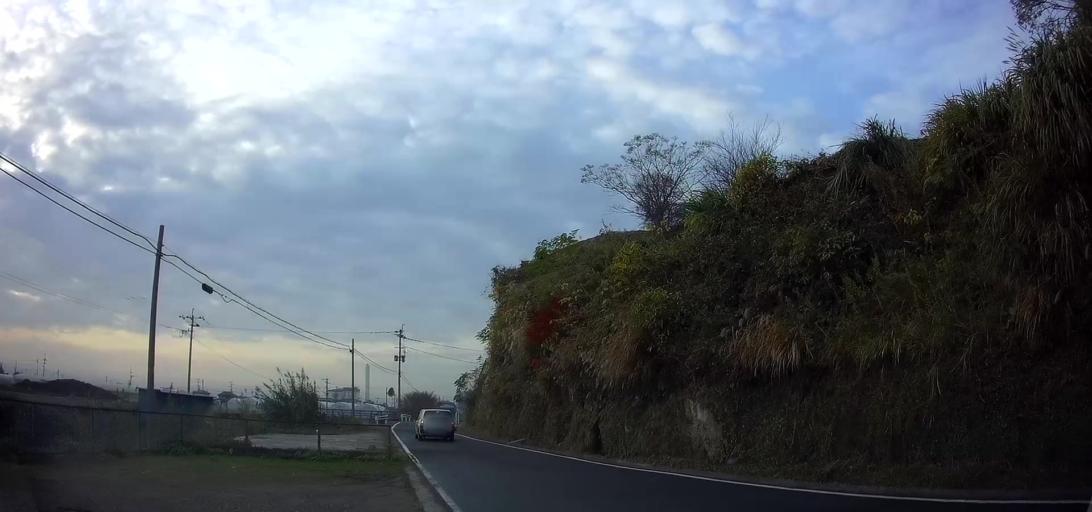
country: JP
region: Nagasaki
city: Shimabara
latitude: 32.6593
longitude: 130.2557
